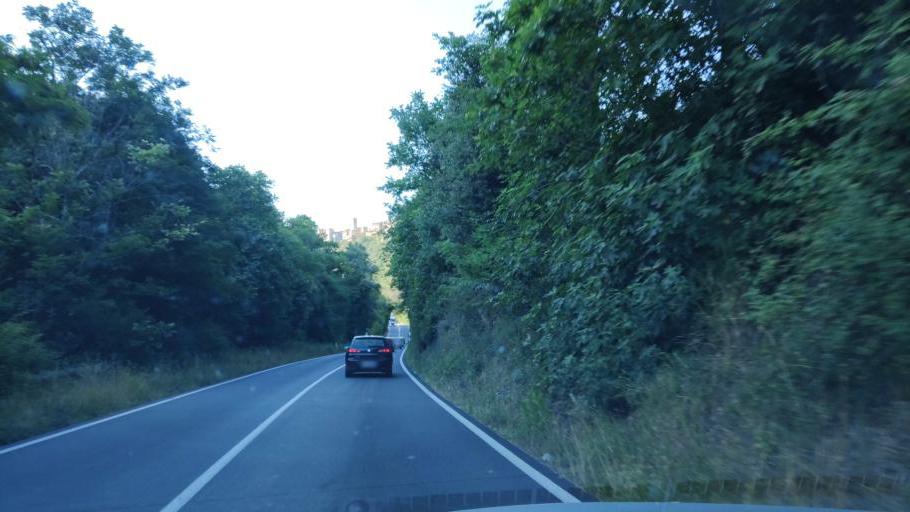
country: IT
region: Umbria
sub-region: Provincia di Terni
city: Narni
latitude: 42.5080
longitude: 12.5143
